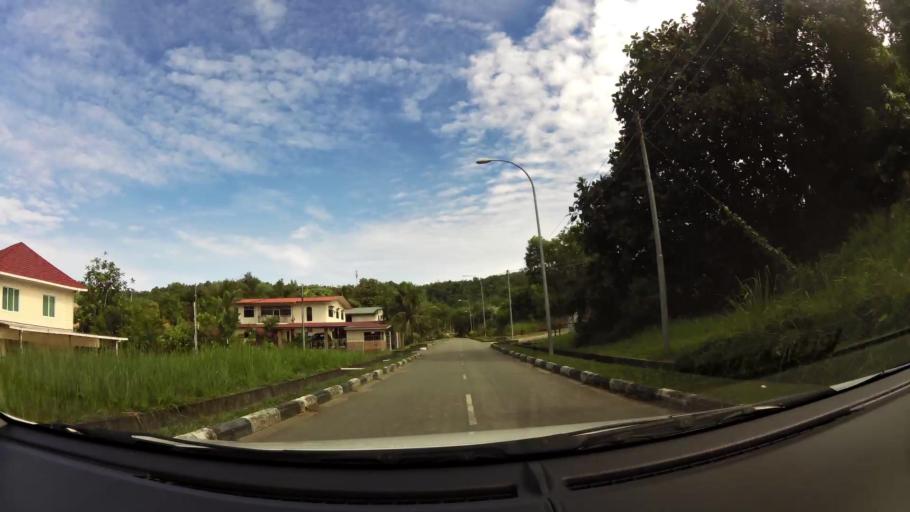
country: BN
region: Brunei and Muara
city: Bandar Seri Begawan
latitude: 4.9070
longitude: 114.9789
